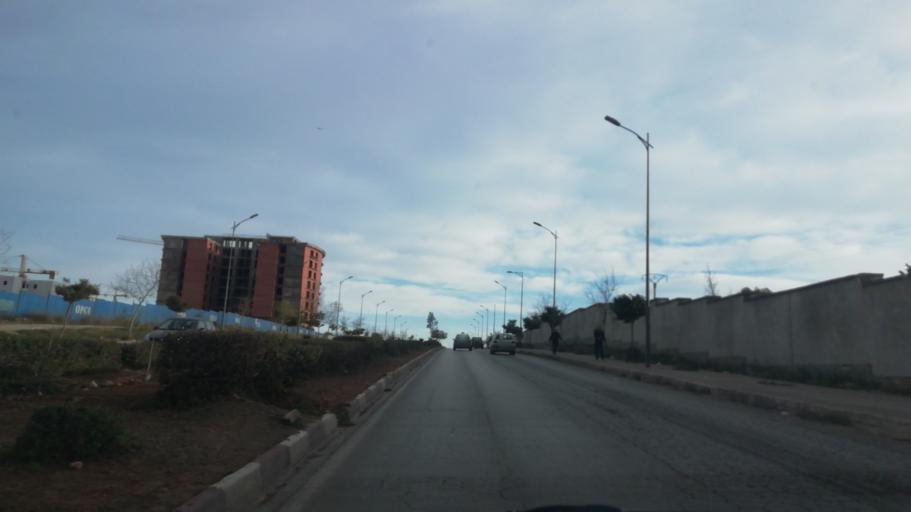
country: DZ
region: Oran
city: Bir el Djir
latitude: 35.7093
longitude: -0.5740
